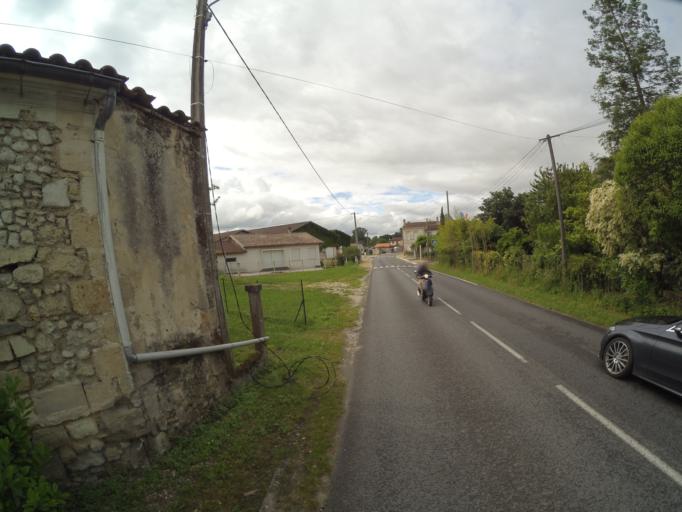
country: FR
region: Aquitaine
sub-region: Departement de la Gironde
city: Soussans
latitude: 45.0583
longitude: -0.7156
